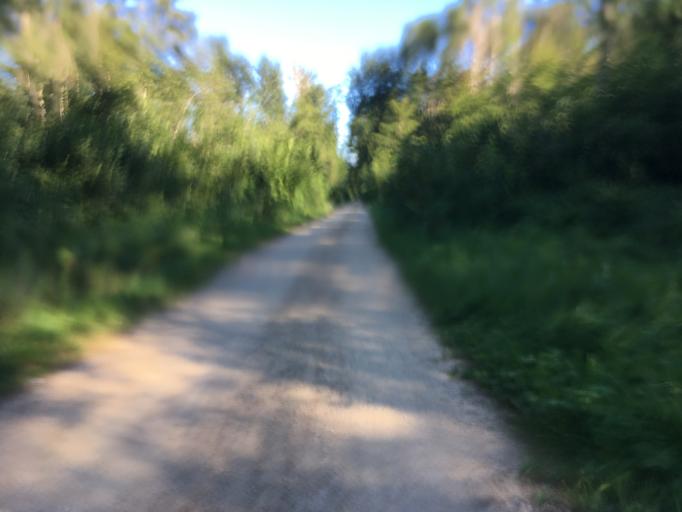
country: CH
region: Fribourg
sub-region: See District
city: Bas-Vully
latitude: 46.9532
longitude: 7.1287
